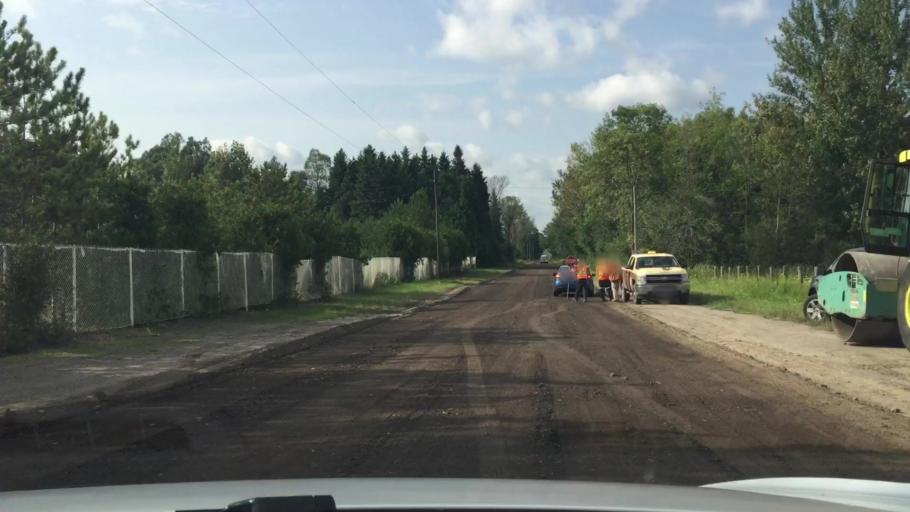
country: CA
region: Ontario
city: Oshawa
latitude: 43.9254
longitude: -78.7407
